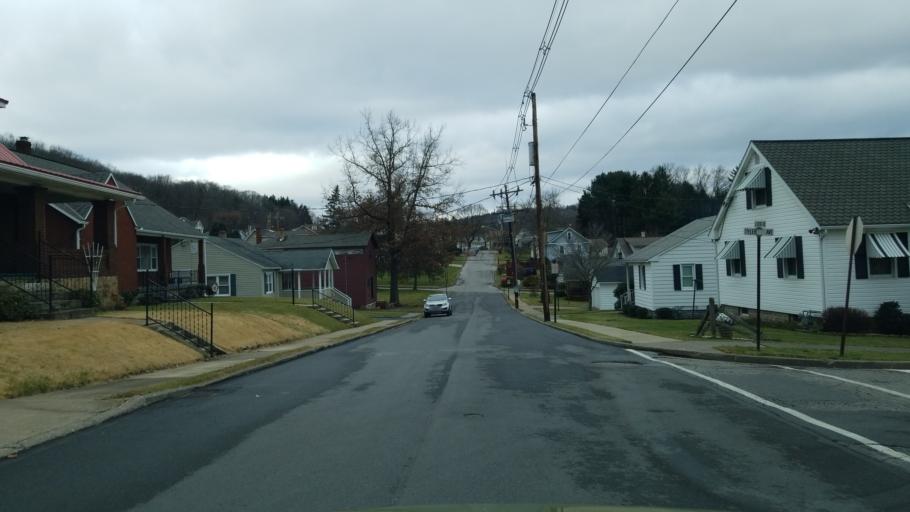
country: US
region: Pennsylvania
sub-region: Clearfield County
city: Clearfield
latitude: 41.0282
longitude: -78.4513
